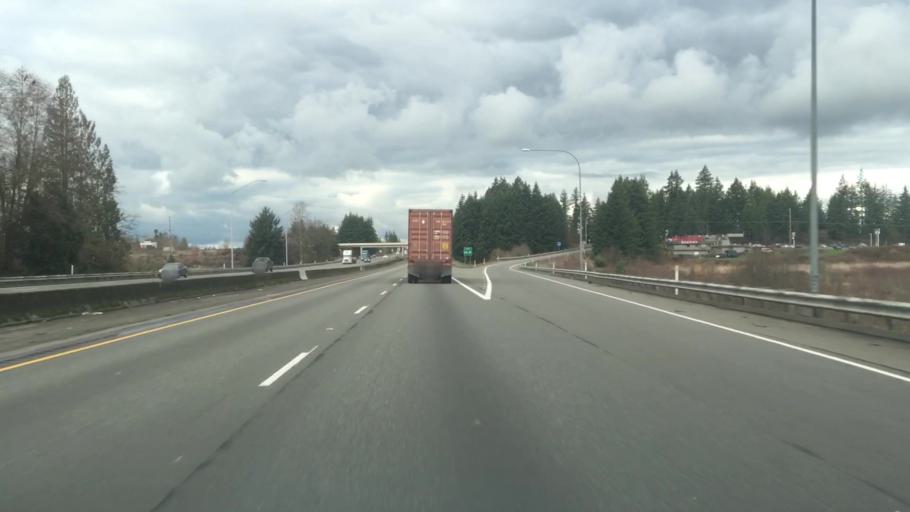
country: US
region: Washington
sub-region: Lewis County
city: Napavine
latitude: 46.5435
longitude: -122.8765
